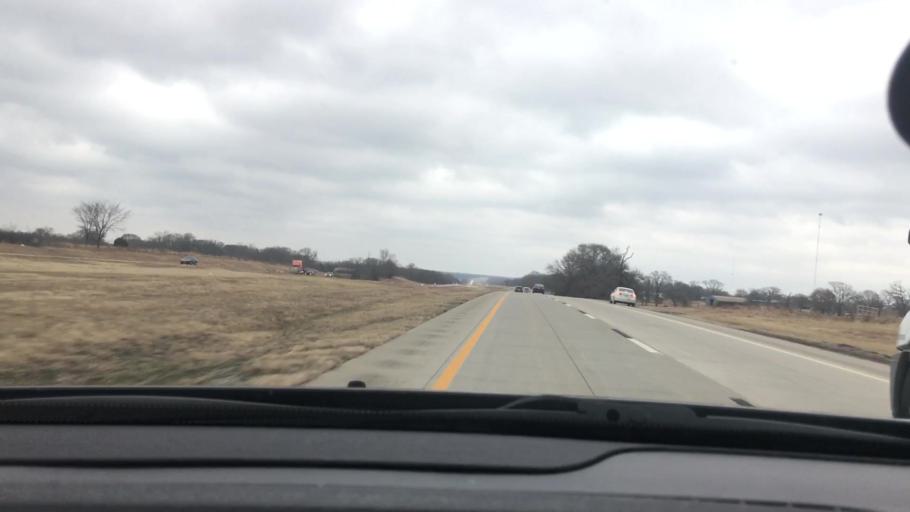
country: US
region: Oklahoma
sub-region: Atoka County
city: Atoka
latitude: 34.2228
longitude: -96.2271
